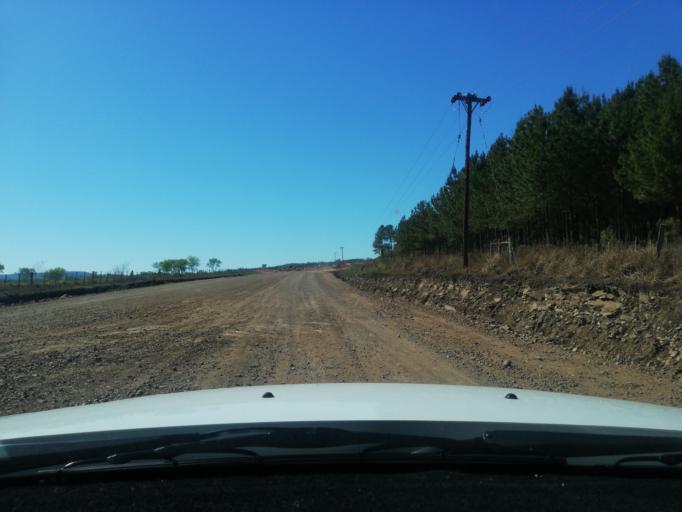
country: AR
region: Misiones
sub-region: Departamento de Candelaria
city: Candelaria
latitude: -27.5293
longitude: -55.7205
